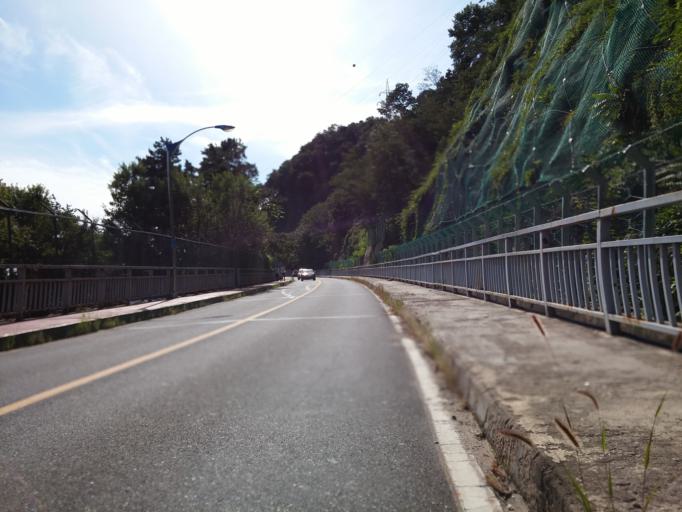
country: KR
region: Daejeon
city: Sintansin
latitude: 36.4800
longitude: 127.4806
